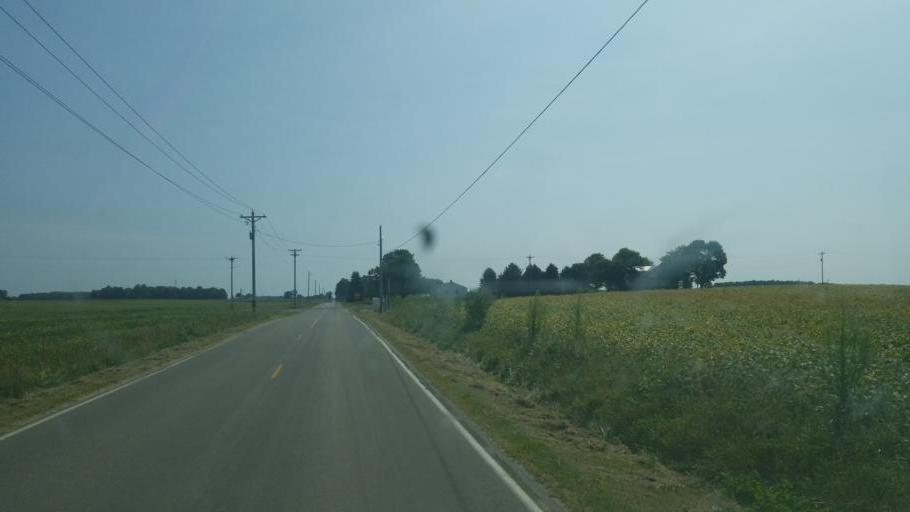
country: US
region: Ohio
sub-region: Crawford County
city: Crestline
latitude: 40.8661
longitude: -82.7441
